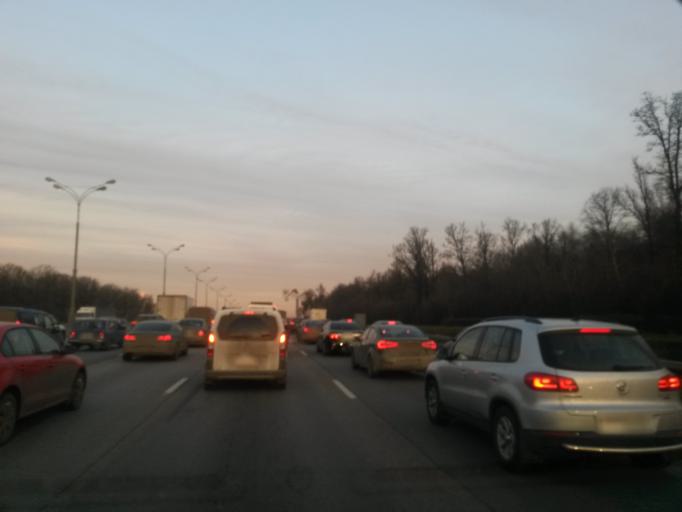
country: RU
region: Moskovskaya
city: Mosrentgen
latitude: 55.6232
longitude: 37.4783
